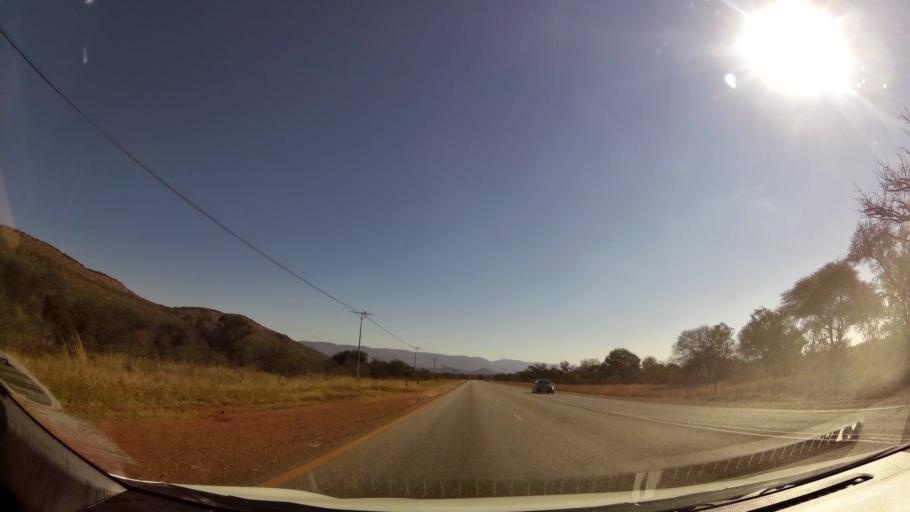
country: ZA
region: Limpopo
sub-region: Waterberg District Municipality
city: Mokopane
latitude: -24.1630
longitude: 29.0590
